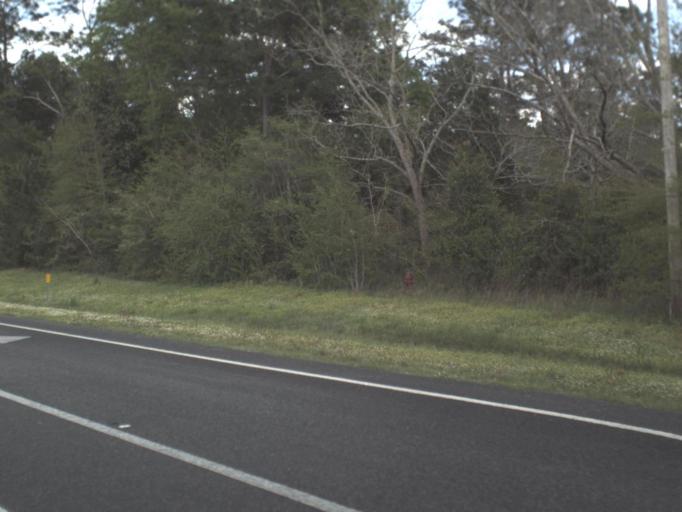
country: US
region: Florida
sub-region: Okaloosa County
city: Crestview
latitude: 30.8181
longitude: -86.5384
